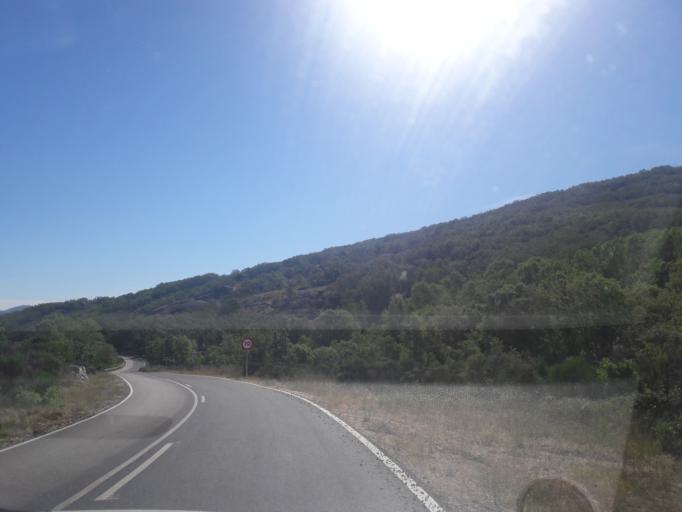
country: ES
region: Castille and Leon
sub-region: Provincia de Salamanca
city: Montemayor del Rio
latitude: 40.3304
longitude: -5.9073
